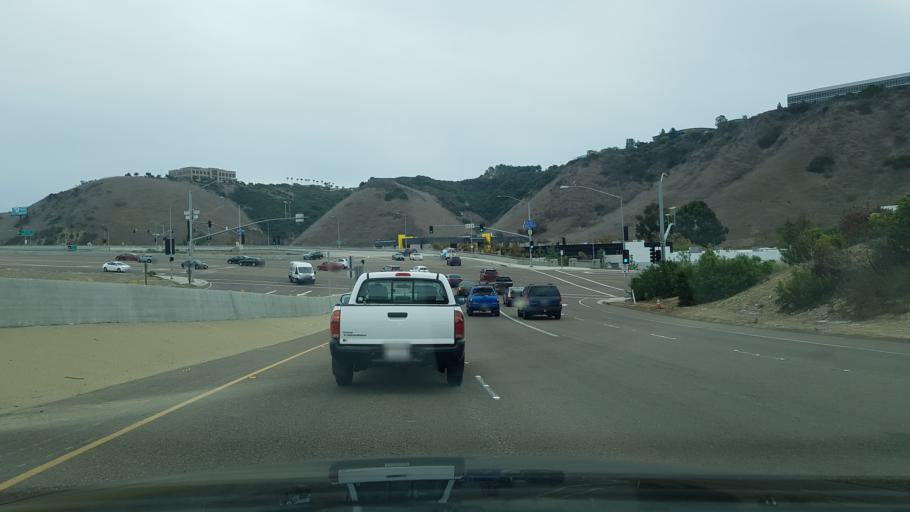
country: US
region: California
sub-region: San Diego County
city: La Jolla
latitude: 32.8911
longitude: -117.2093
